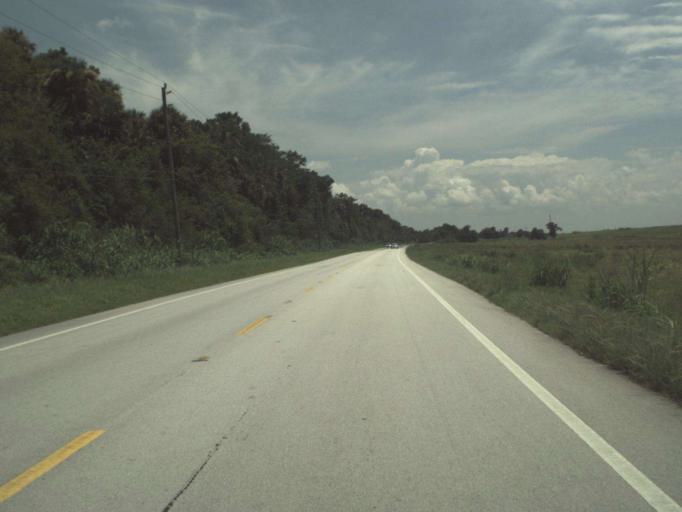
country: US
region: Florida
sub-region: Martin County
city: Indiantown
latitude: 26.9640
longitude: -80.6103
